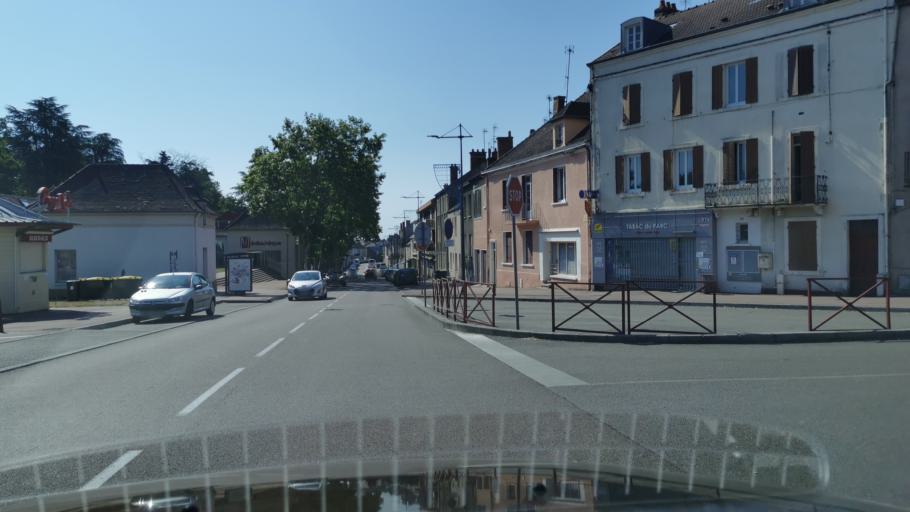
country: FR
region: Bourgogne
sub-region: Departement de Saone-et-Loire
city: Le Creusot
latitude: 46.8016
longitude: 4.4198
